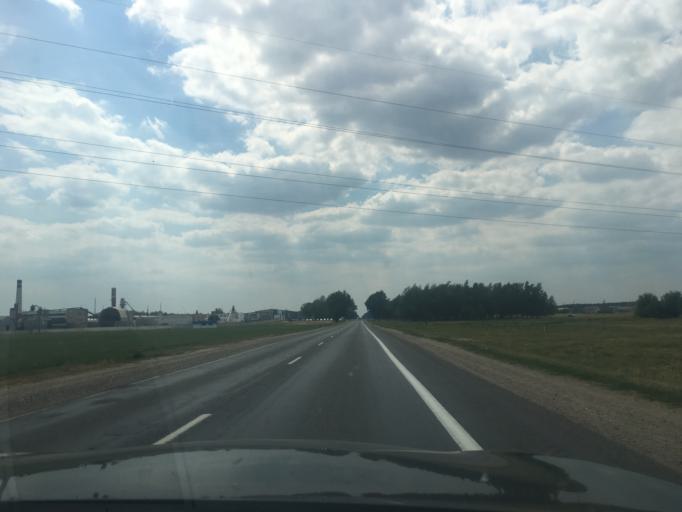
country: BY
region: Brest
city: Pruzhany
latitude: 52.5448
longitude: 24.4563
